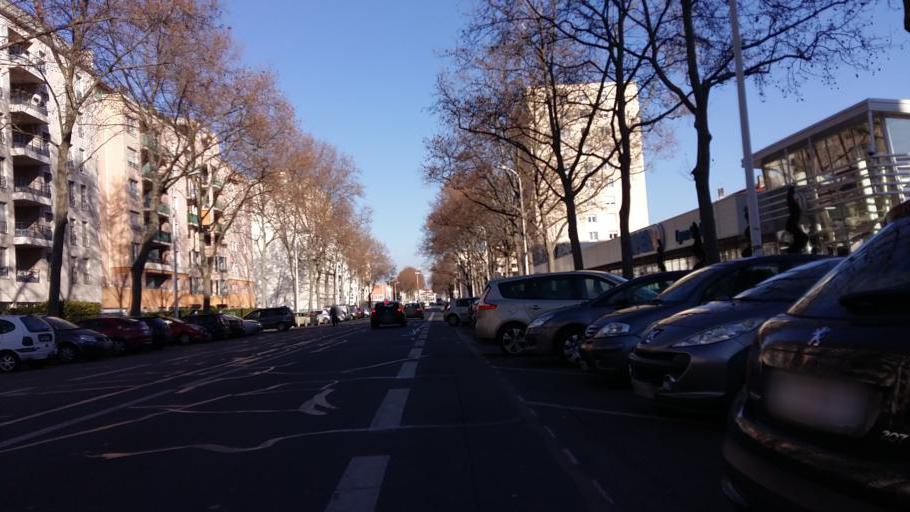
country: FR
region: Rhone-Alpes
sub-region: Departement du Rhone
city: Lyon
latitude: 45.7363
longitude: 4.8281
